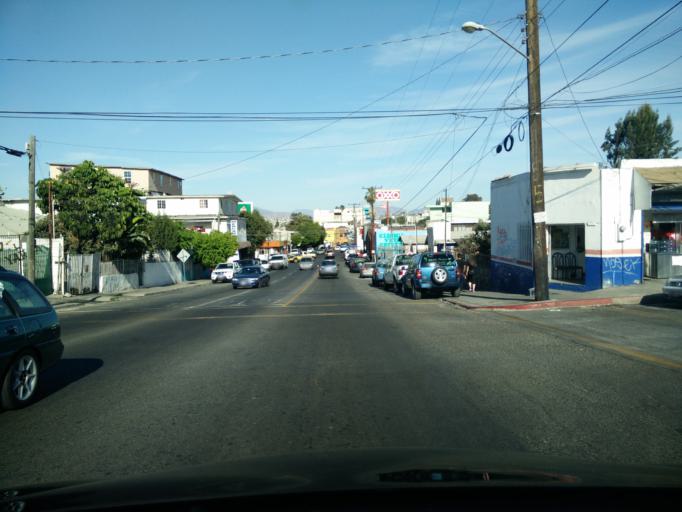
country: MX
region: Baja California
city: Tijuana
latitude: 32.5265
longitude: -117.0501
